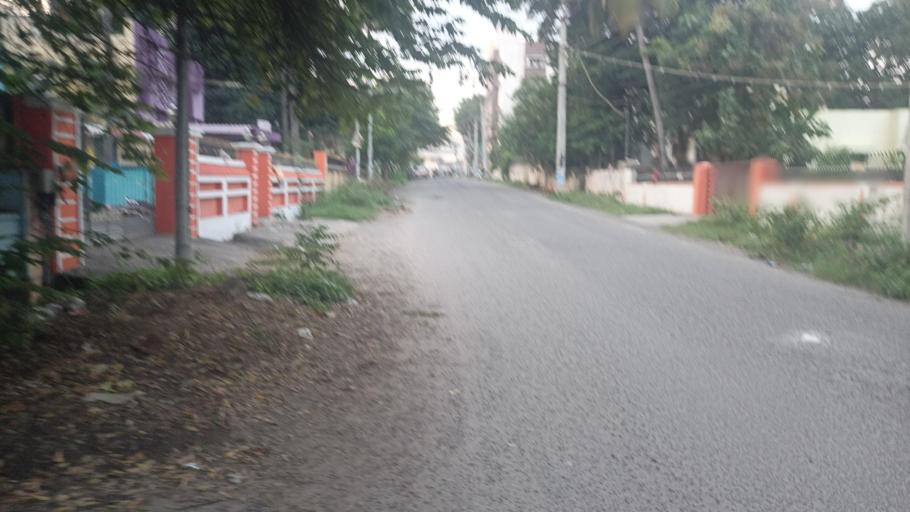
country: IN
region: Tamil Nadu
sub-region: Salem
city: Salem
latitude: 11.6731
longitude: 78.1189
